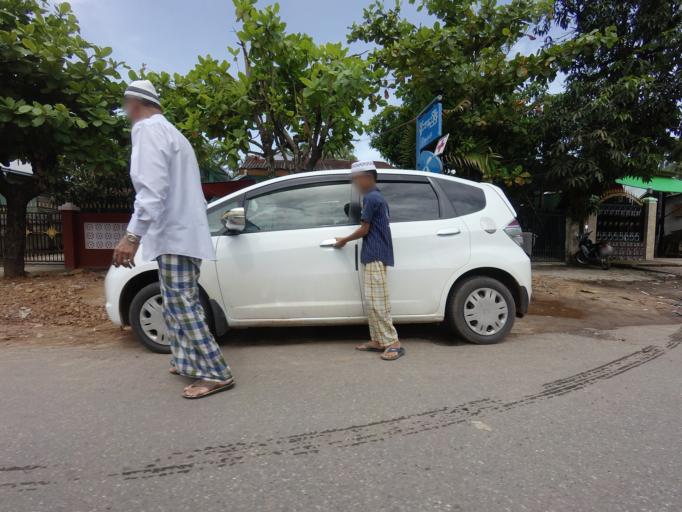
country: MM
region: Mon
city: Mawlamyine
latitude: 16.4525
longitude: 97.6271
